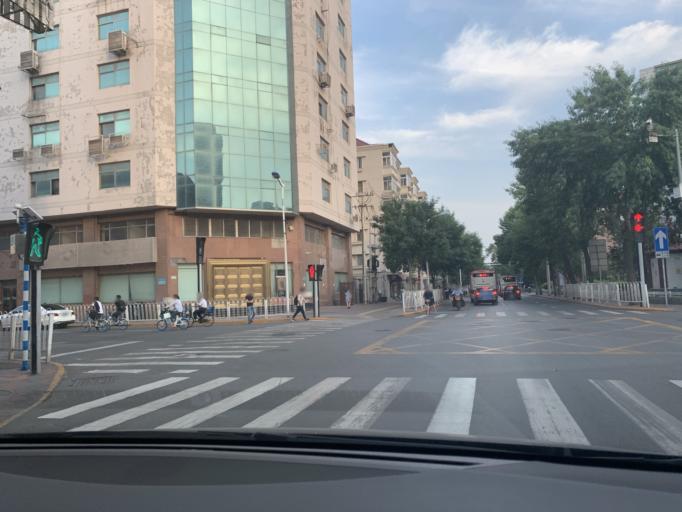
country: CN
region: Tianjin Shi
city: Quanyechang
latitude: 39.1183
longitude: 117.1980
